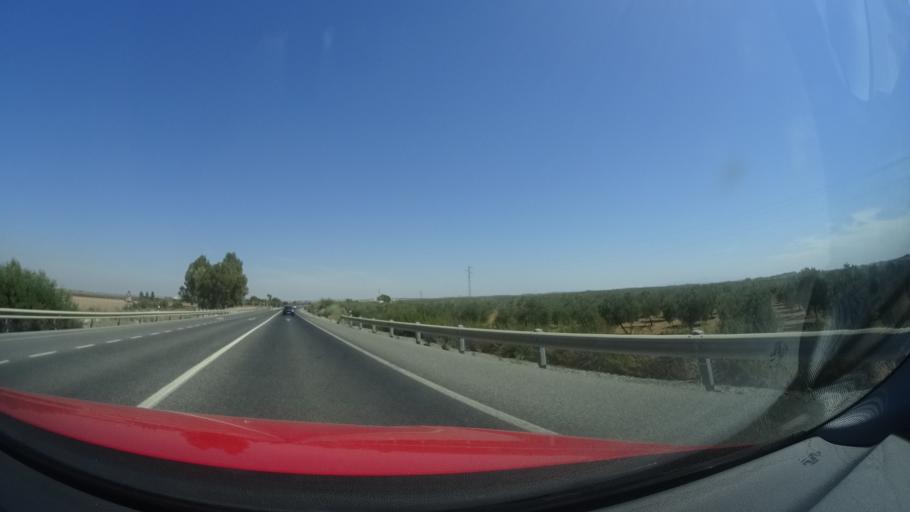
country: ES
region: Andalusia
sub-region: Provincia de Sevilla
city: Las Cabezas de San Juan
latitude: 36.9089
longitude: -5.9676
